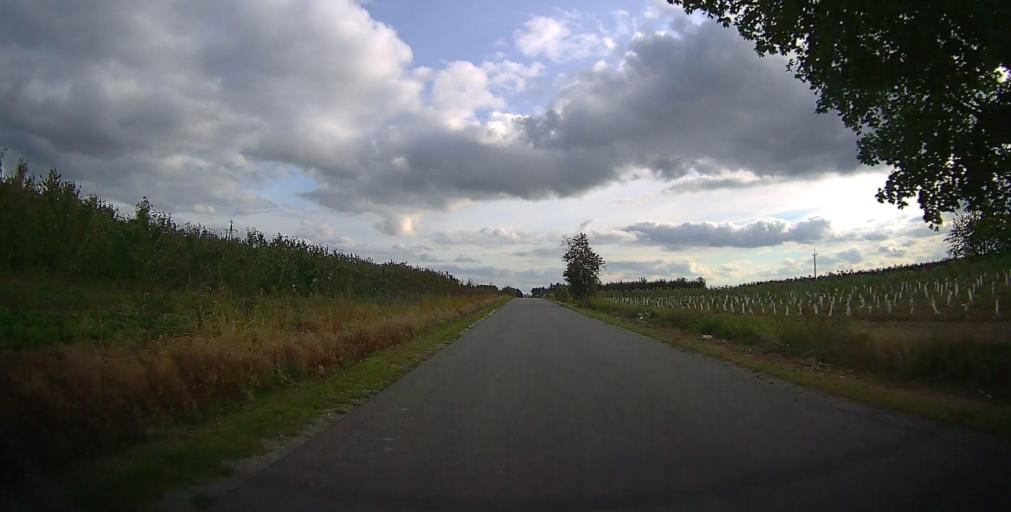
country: PL
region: Masovian Voivodeship
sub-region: Powiat bialobrzeski
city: Promna
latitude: 51.7376
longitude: 20.9652
